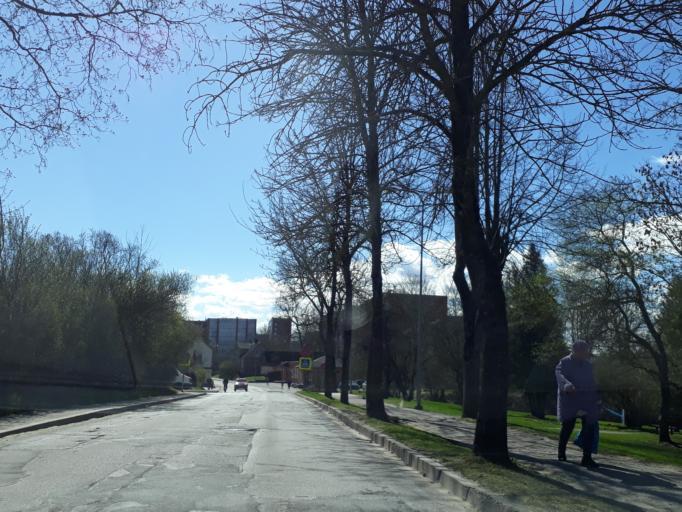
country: LV
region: Dobeles Rajons
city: Dobele
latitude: 56.6206
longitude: 23.2800
